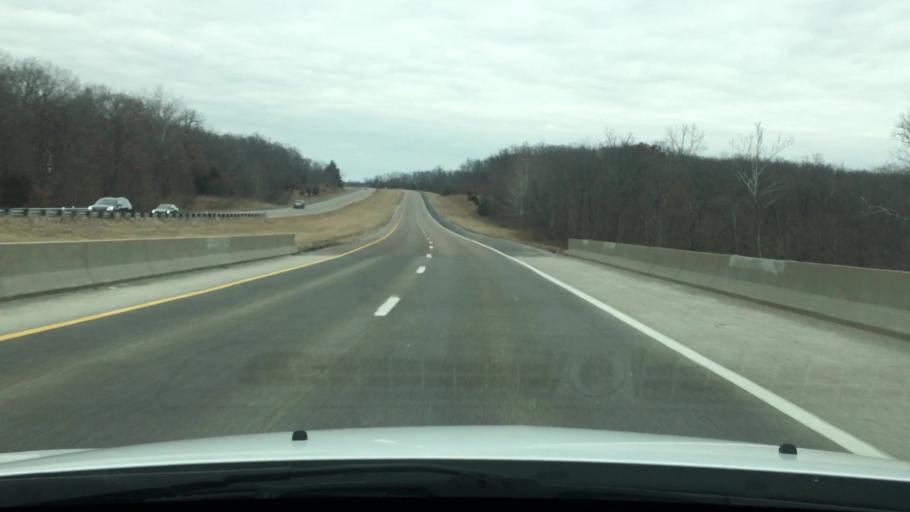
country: US
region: Missouri
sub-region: Callaway County
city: Fulton
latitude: 38.9708
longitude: -91.8982
